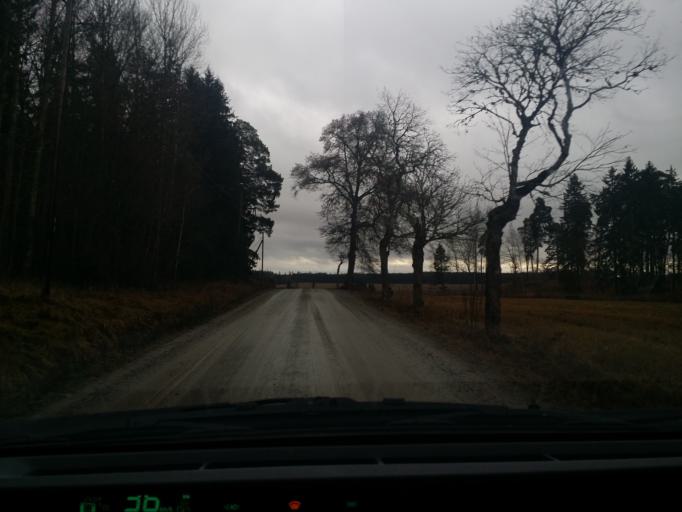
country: SE
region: Vaestmanland
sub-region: Vasteras
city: Skultuna
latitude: 59.7817
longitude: 16.3884
